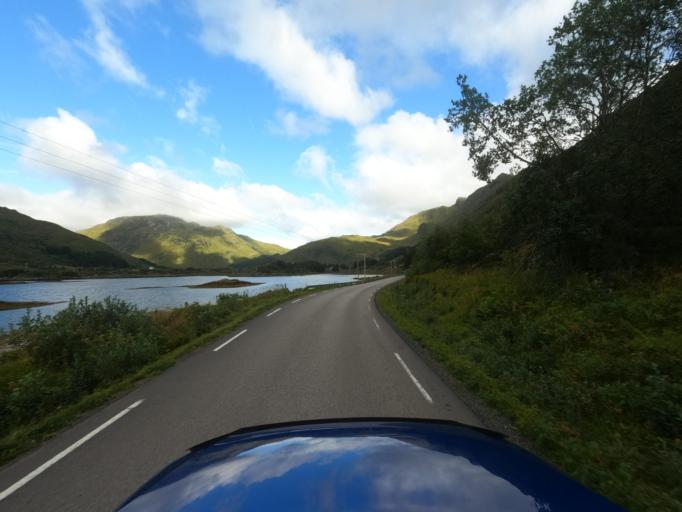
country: NO
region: Nordland
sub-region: Vestvagoy
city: Evjen
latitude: 68.1922
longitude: 13.8931
